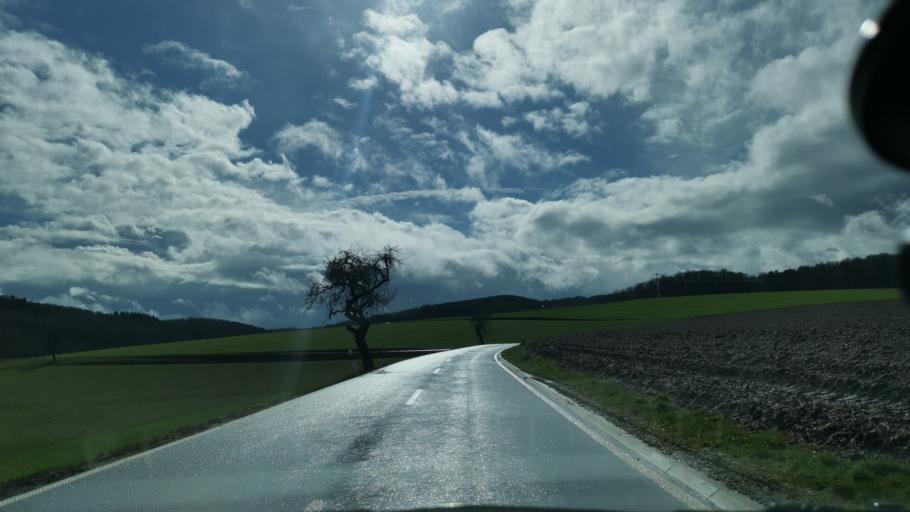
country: DE
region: Hesse
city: Waldkappel
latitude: 51.1222
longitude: 9.8727
